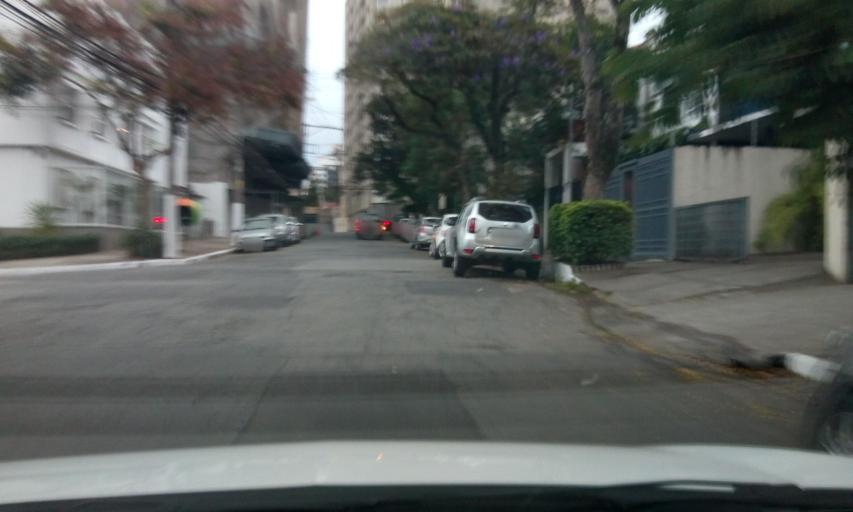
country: BR
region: Sao Paulo
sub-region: Sao Paulo
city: Sao Paulo
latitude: -23.5891
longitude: -46.6439
